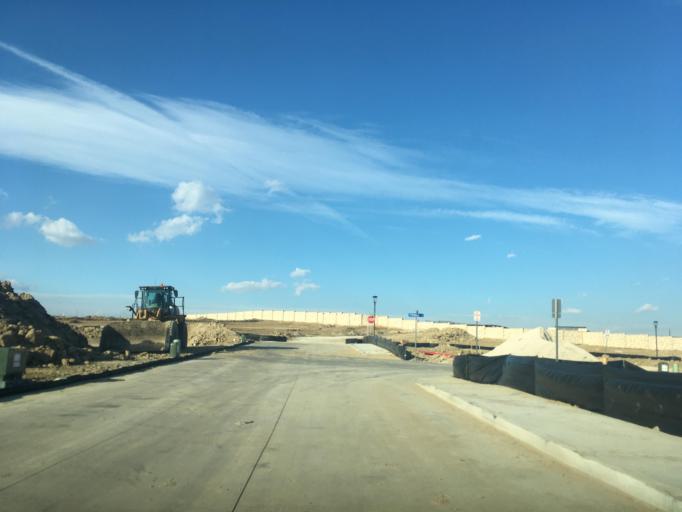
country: US
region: Colorado
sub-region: Boulder County
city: Superior
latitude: 39.9483
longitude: -105.1542
